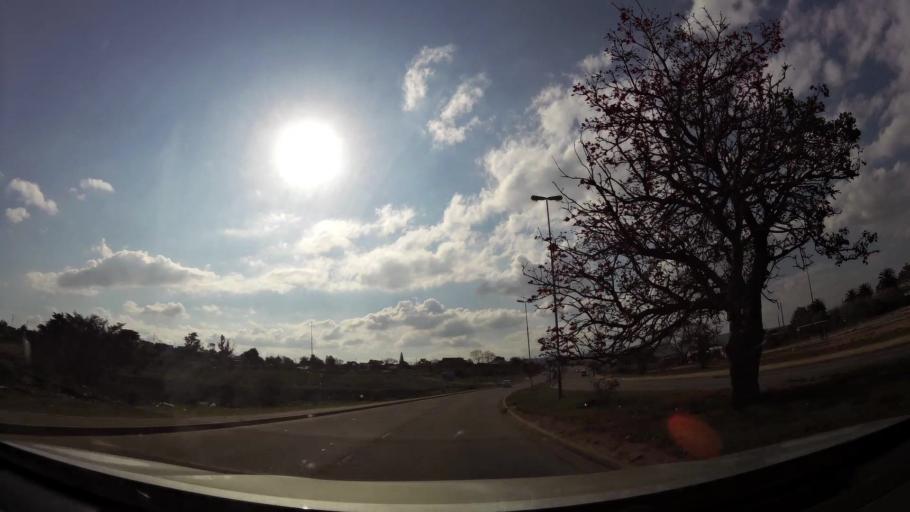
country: ZA
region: Eastern Cape
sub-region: Nelson Mandela Bay Metropolitan Municipality
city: Uitenhage
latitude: -33.7585
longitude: 25.3881
